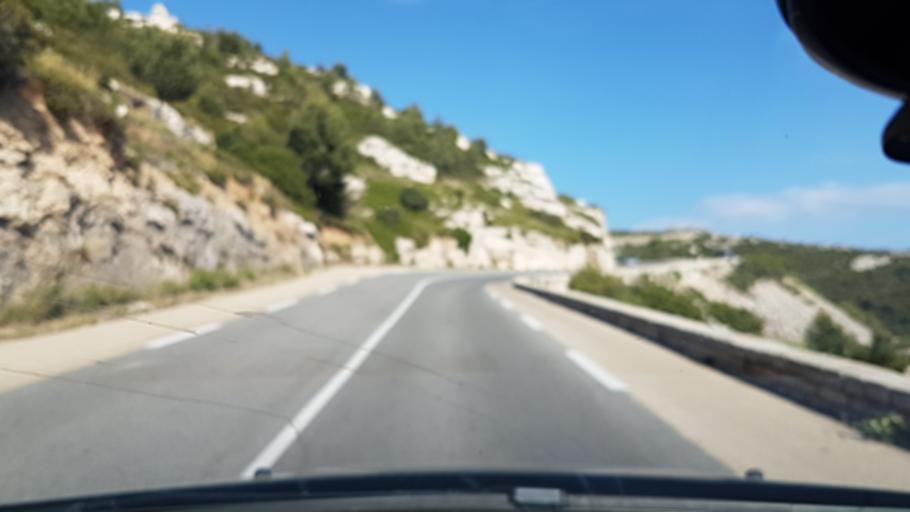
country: FR
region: Provence-Alpes-Cote d'Azur
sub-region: Departement des Bouches-du-Rhone
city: Marseille 09
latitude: 43.2430
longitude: 5.4456
